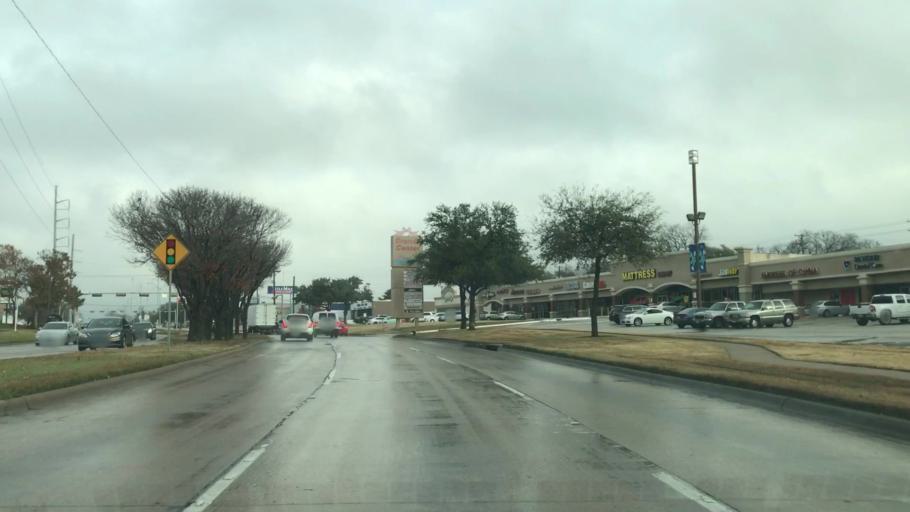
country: US
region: Texas
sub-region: Dallas County
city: Irving
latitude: 32.8421
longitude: -96.9926
